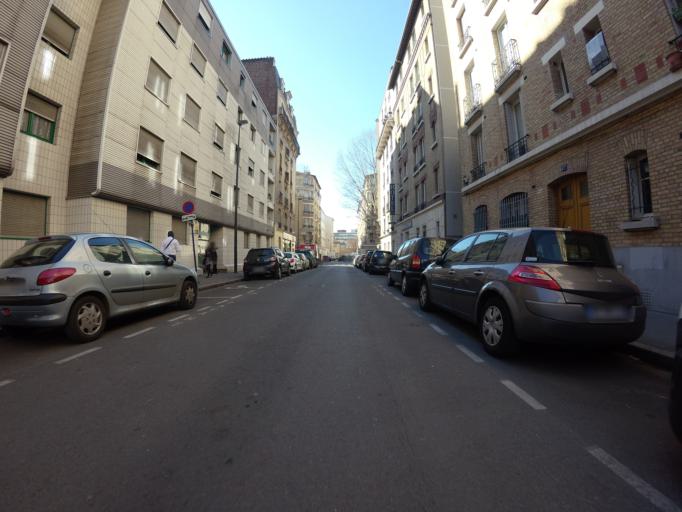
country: FR
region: Ile-de-France
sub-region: Departement des Hauts-de-Seine
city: Clichy
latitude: 48.9024
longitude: 2.3148
